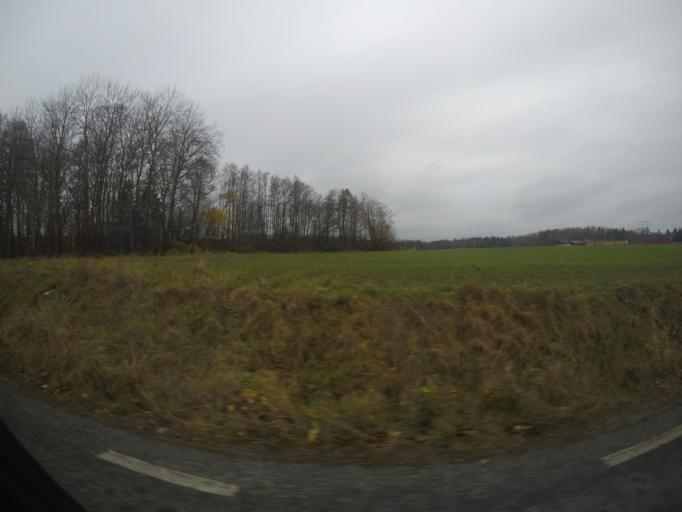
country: SE
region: Vaestmanland
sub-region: Vasteras
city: Skultuna
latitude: 59.7149
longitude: 16.4086
